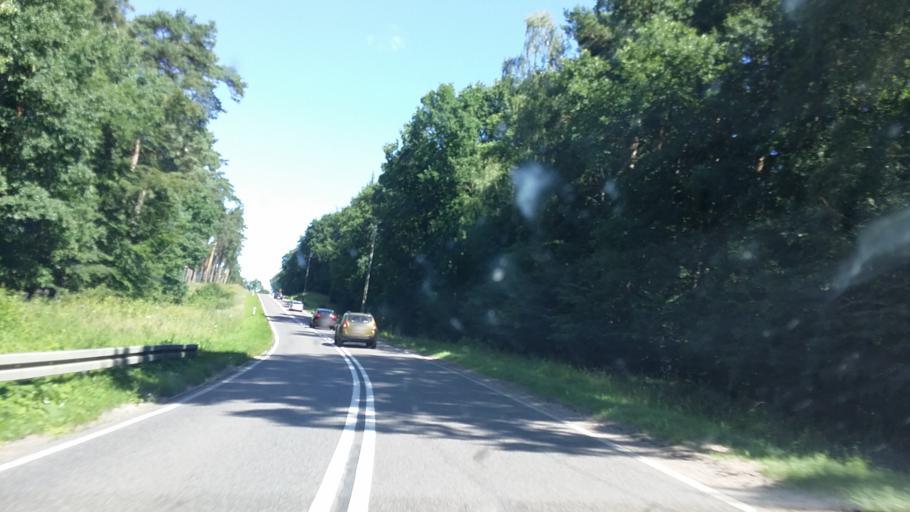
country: PL
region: West Pomeranian Voivodeship
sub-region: Powiat drawski
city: Drawsko Pomorskie
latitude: 53.4597
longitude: 15.8266
